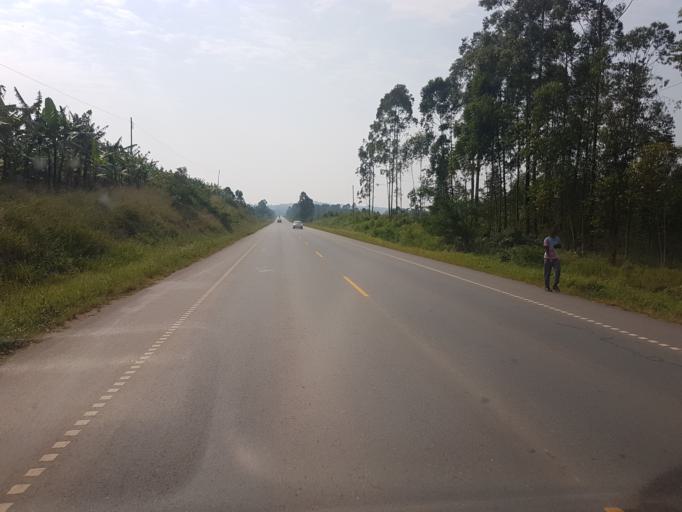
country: UG
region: Western Region
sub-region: Mbarara District
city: Bwizibwera
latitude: -0.6428
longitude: 30.5641
